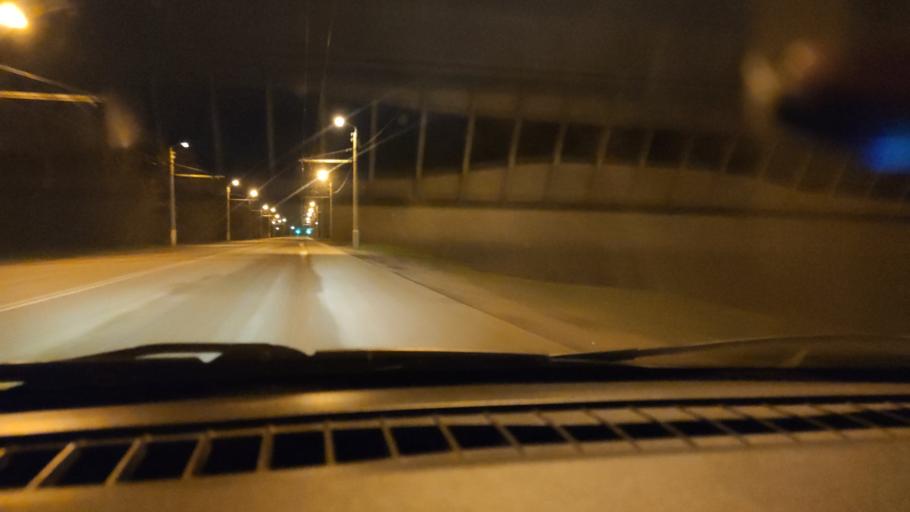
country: RU
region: Bashkortostan
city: Sterlitamak
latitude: 53.6586
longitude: 55.9230
